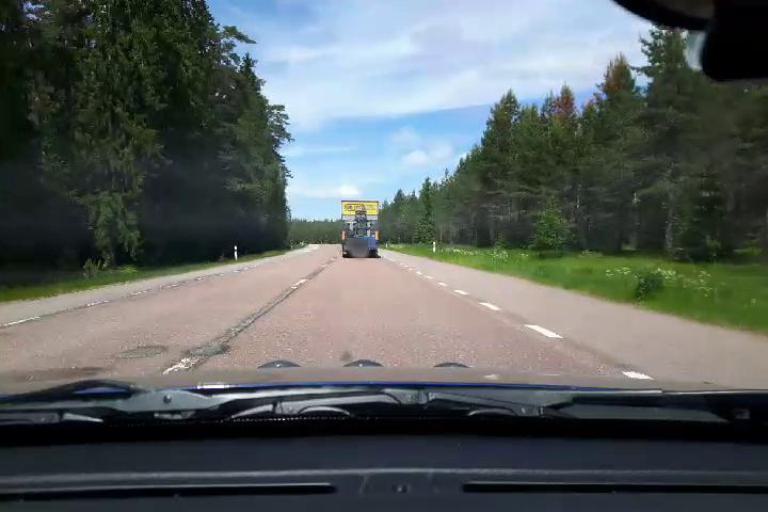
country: SE
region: Uppsala
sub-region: Osthammars Kommun
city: Bjorklinge
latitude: 60.1278
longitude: 17.5095
